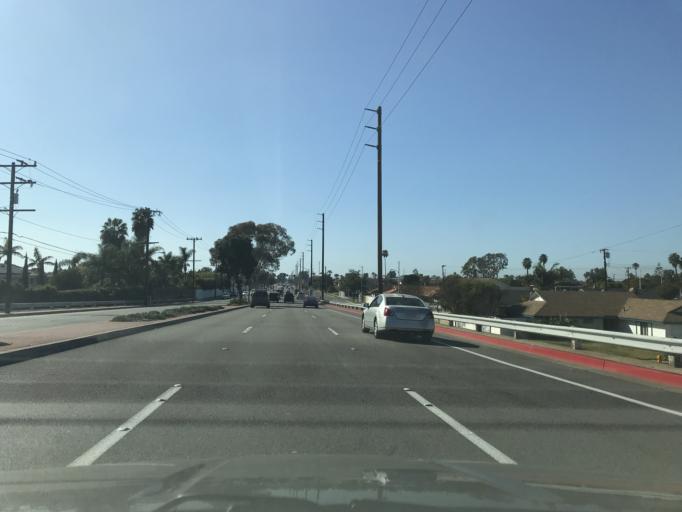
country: US
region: California
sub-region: Orange County
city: Fountain Valley
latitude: 33.6725
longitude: -117.9469
